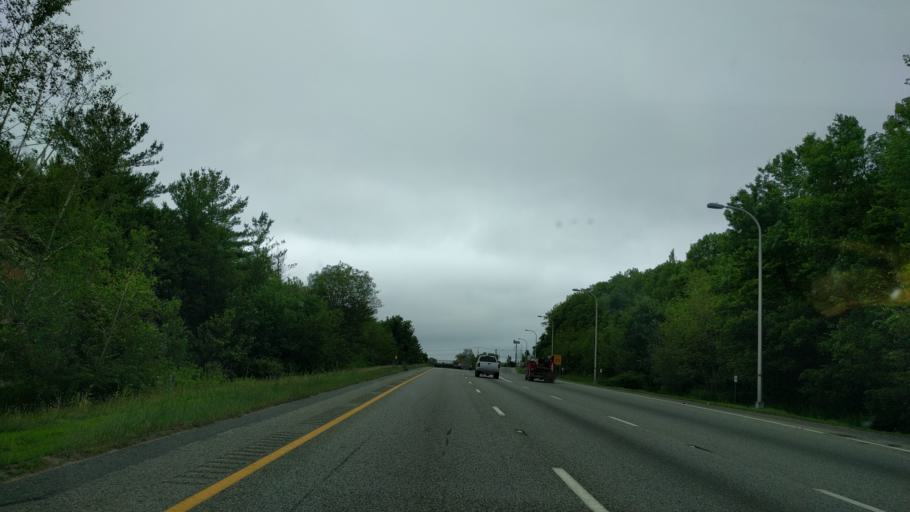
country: US
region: Rhode Island
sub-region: Providence County
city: Johnston
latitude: 41.8085
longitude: -71.5102
